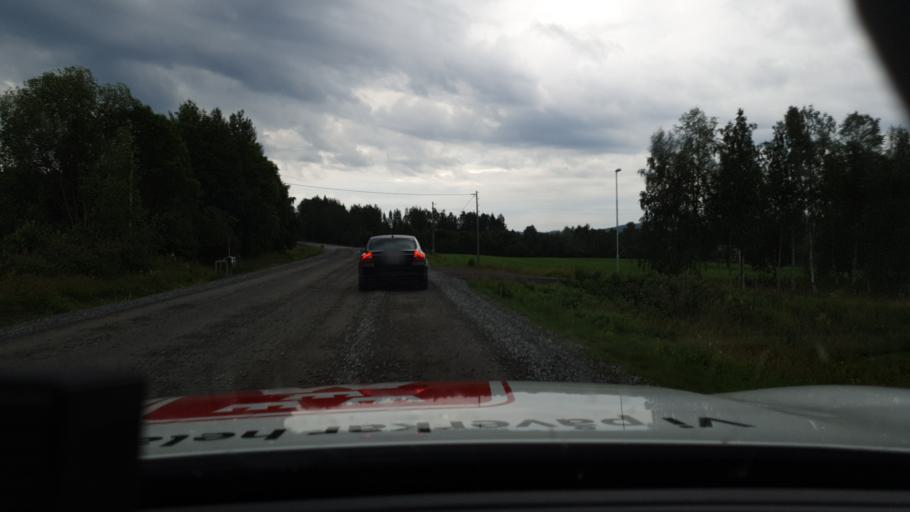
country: SE
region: Norrbotten
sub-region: Bodens Kommun
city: Boden
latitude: 65.8649
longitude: 21.4188
